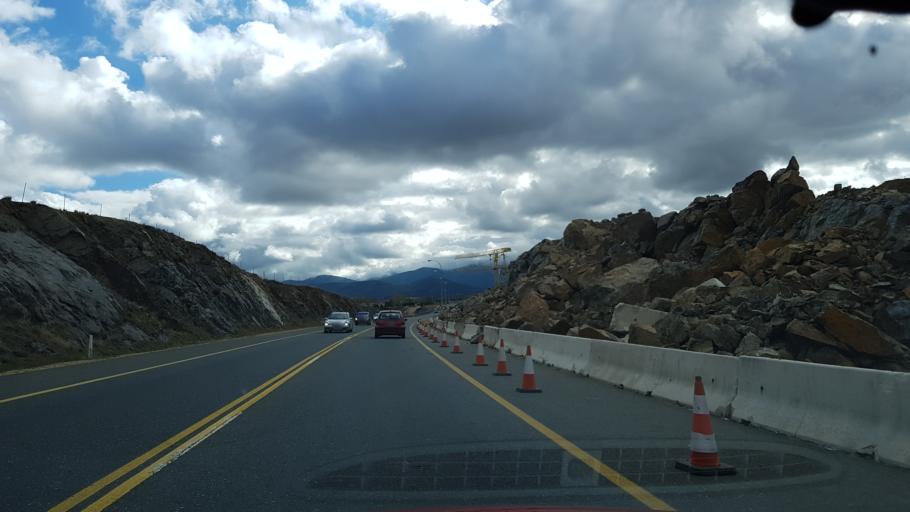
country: ES
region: Castille and Leon
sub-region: Provincia de Segovia
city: San Cristobal de Segovia
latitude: 40.9429
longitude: -4.0856
